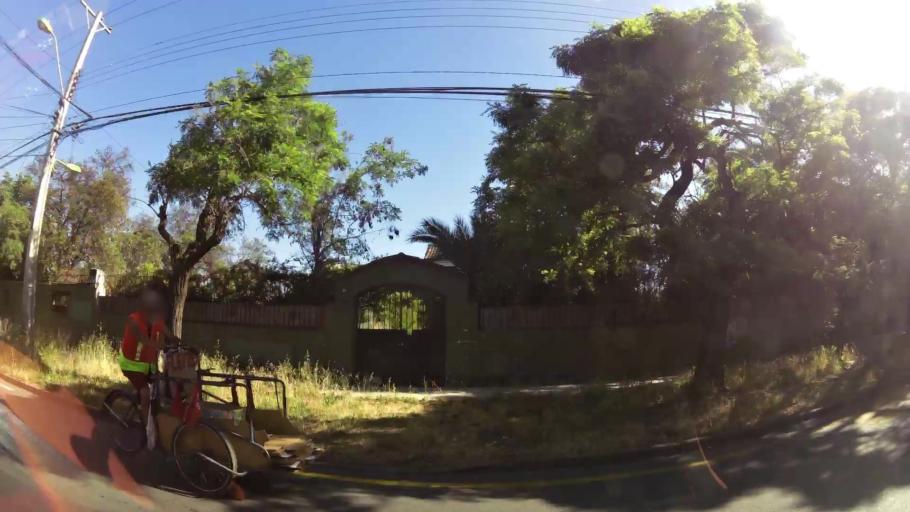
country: CL
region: Santiago Metropolitan
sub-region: Provincia de Maipo
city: San Bernardo
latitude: -33.5504
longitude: -70.6766
